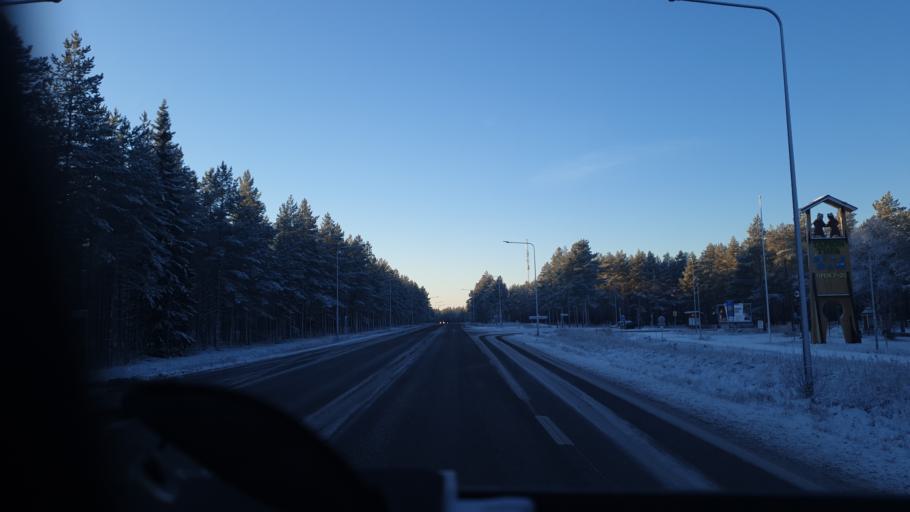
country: FI
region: Northern Ostrobothnia
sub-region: Ylivieska
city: Kalajoki
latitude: 64.2410
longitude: 23.8458
